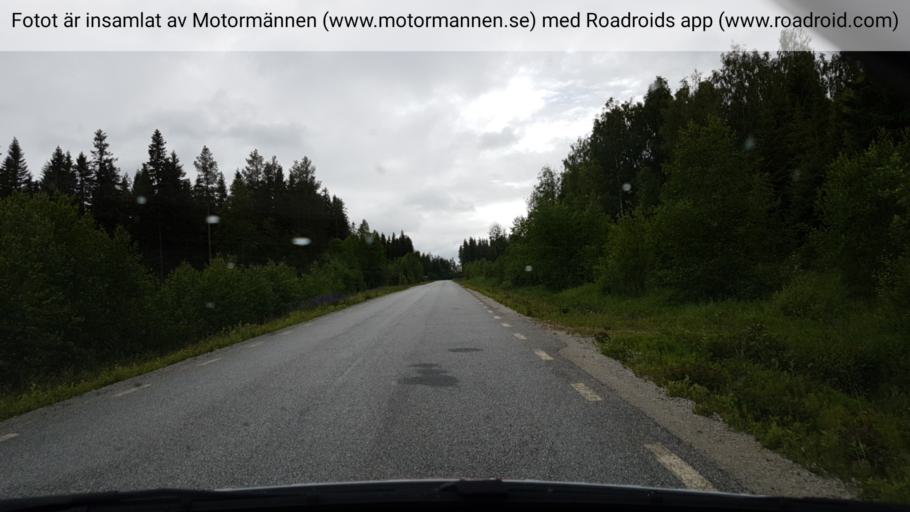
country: SE
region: Vaesterbotten
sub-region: Bjurholms Kommun
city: Bjurholm
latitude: 63.9866
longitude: 19.3344
